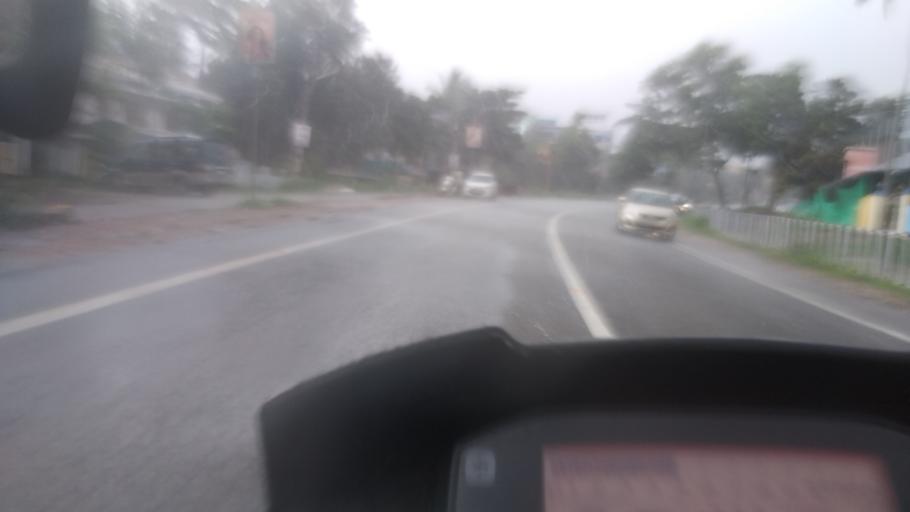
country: IN
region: Kerala
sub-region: Thiruvananthapuram
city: Attingal
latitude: 8.7124
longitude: 76.8117
